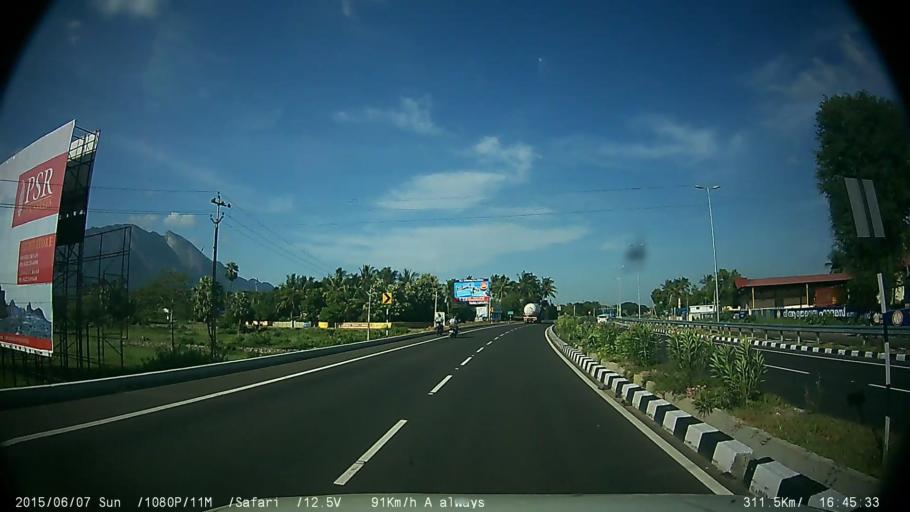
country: IN
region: Kerala
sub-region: Palakkad district
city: Palakkad
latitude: 10.7993
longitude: 76.7463
